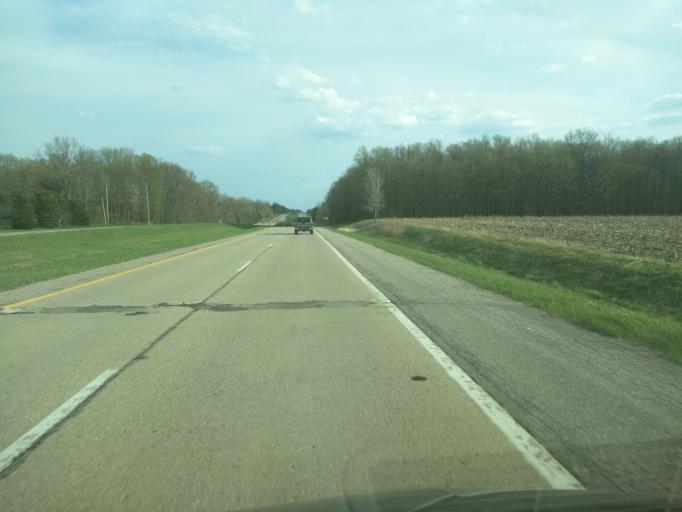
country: US
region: Michigan
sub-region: Eaton County
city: Dimondale
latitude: 42.6351
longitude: -84.6232
